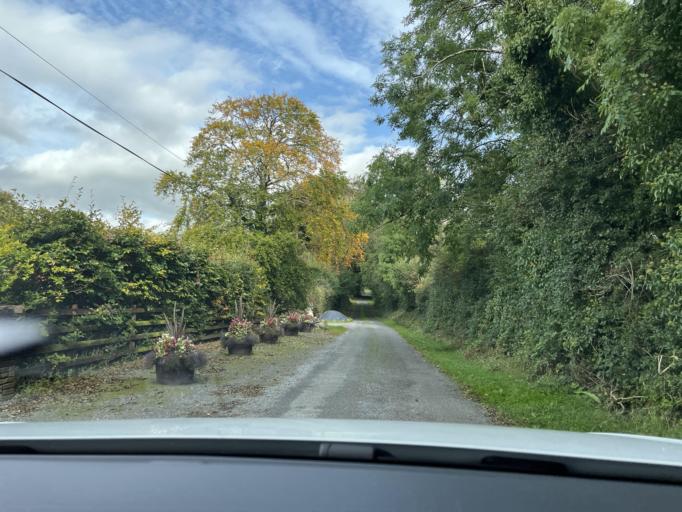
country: IE
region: Connaught
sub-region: County Leitrim
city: Carrick-on-Shannon
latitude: 53.9705
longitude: -8.0770
